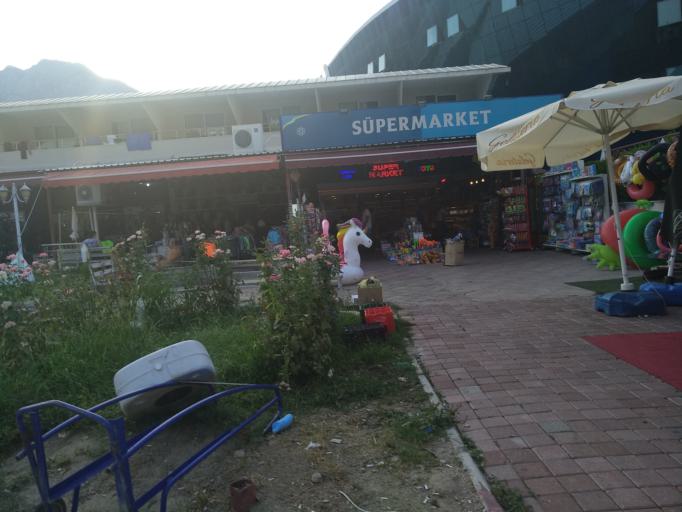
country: TR
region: Antalya
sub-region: Kemer
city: Goeynuek
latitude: 36.6635
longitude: 30.5600
